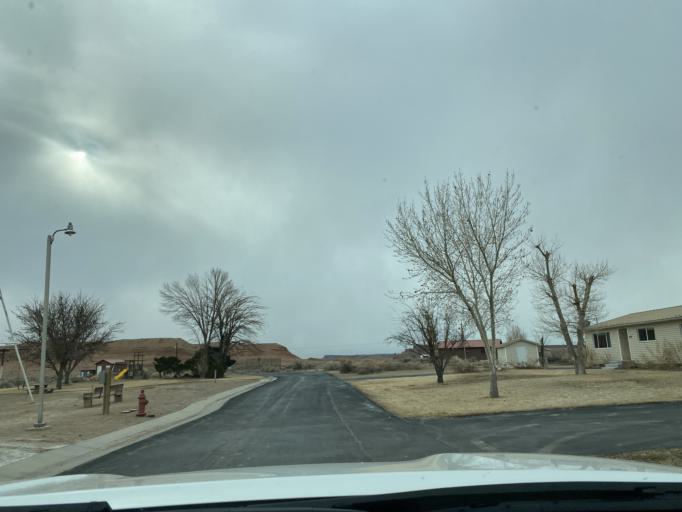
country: US
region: Utah
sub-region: Emery County
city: Ferron
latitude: 38.3647
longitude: -110.7180
